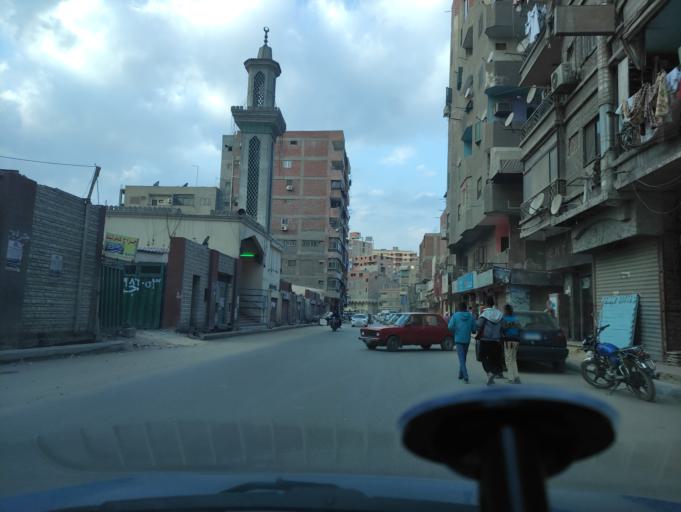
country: EG
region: Muhafazat al Qalyubiyah
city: Al Khankah
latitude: 30.1311
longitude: 31.3609
